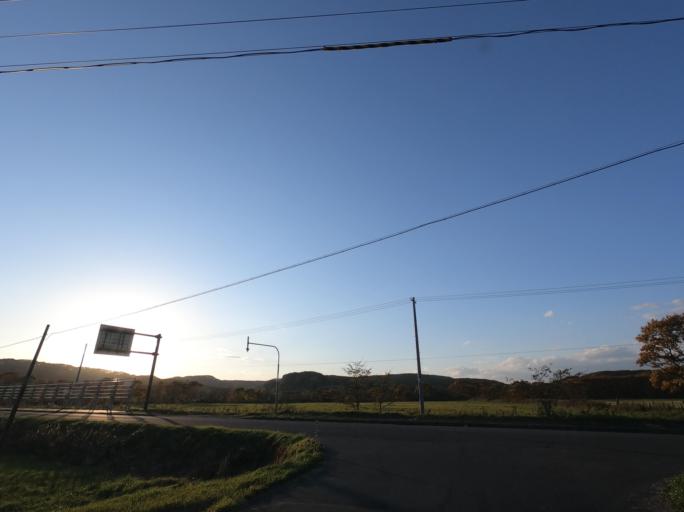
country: JP
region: Hokkaido
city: Kushiro
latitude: 43.2017
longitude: 144.4249
